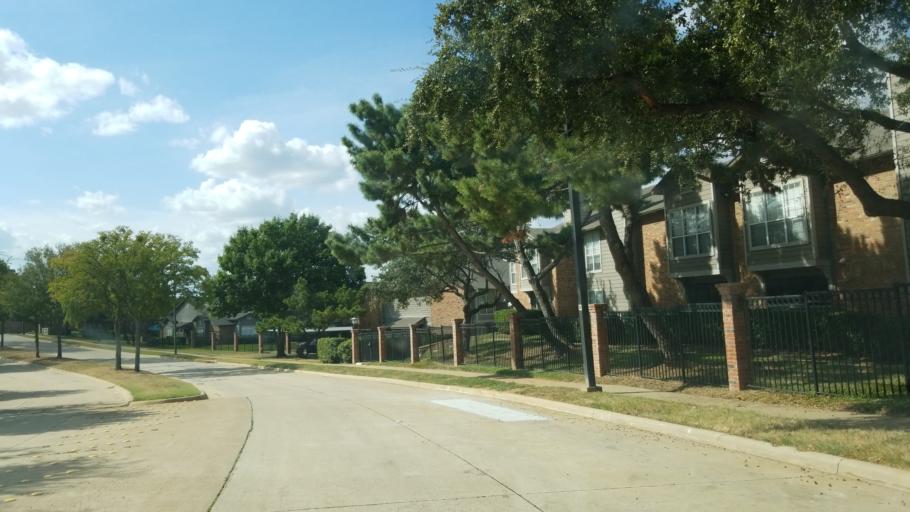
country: US
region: Texas
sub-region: Tarrant County
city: Euless
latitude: 32.8613
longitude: -97.0722
